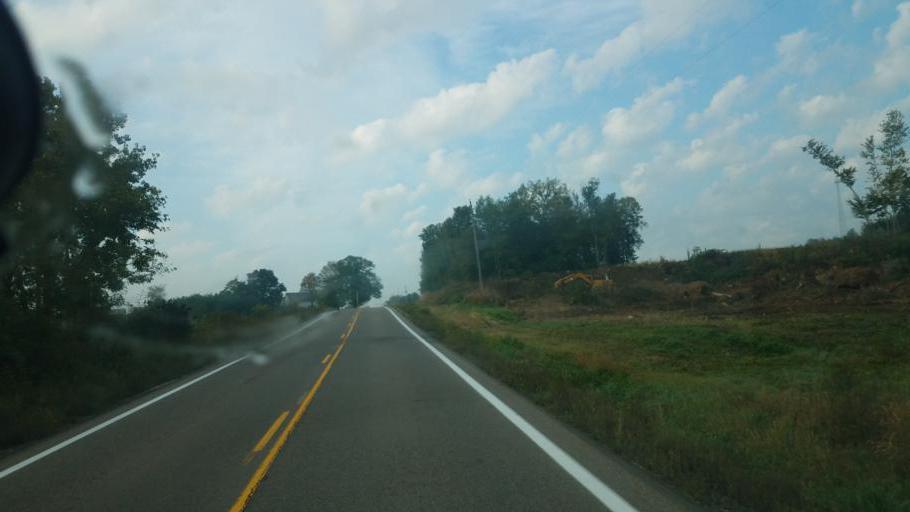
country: US
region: Ohio
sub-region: Knox County
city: Gambier
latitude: 40.2955
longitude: -82.3360
